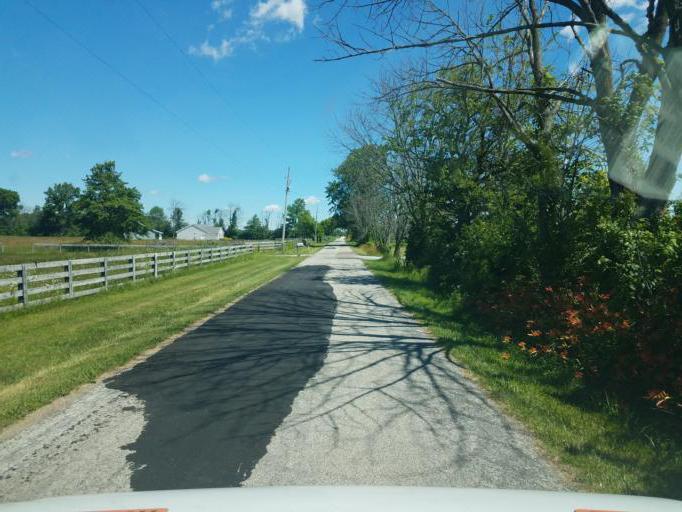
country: US
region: Ohio
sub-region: Morrow County
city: Cardington
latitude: 40.5250
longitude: -82.9341
